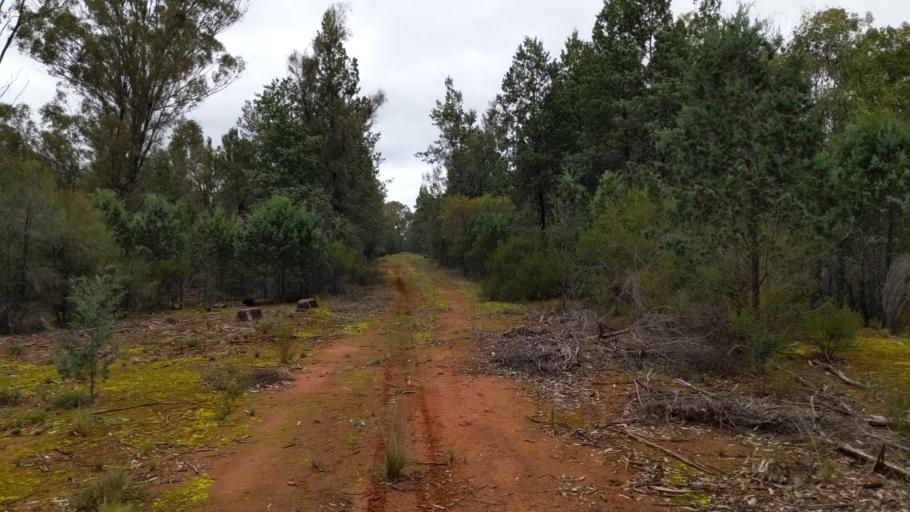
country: AU
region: New South Wales
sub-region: Coolamon
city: Coolamon
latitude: -34.8505
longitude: 146.9319
